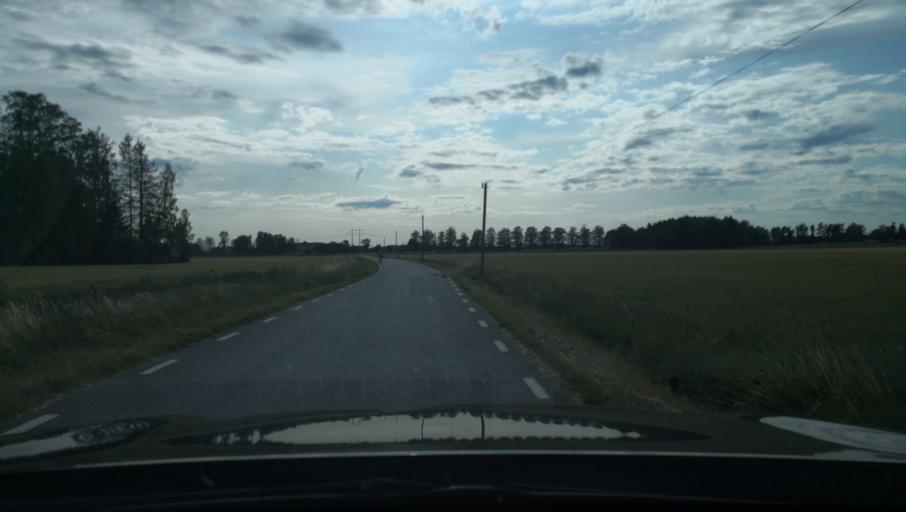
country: SE
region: Uppsala
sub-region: Enkopings Kommun
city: Orsundsbro
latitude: 59.6928
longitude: 17.3430
